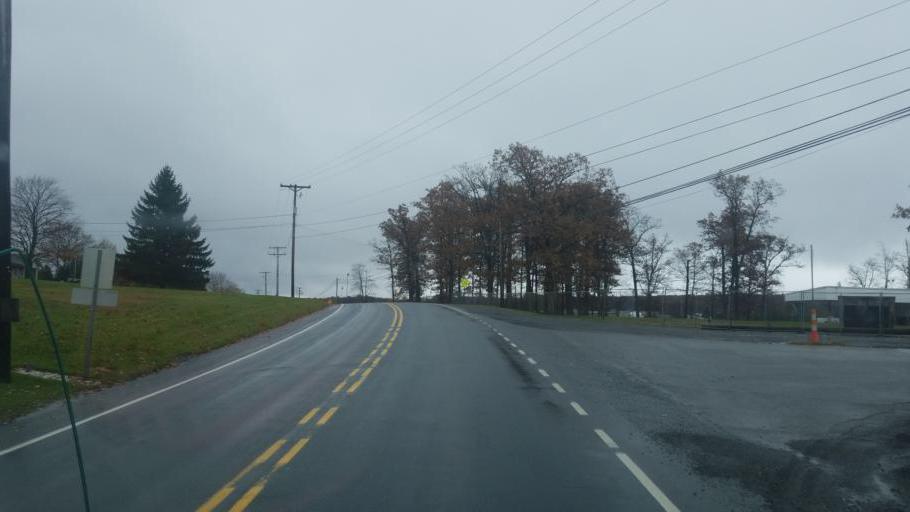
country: US
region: Pennsylvania
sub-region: Centre County
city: Milesburg
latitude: 41.0261
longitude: -77.9446
